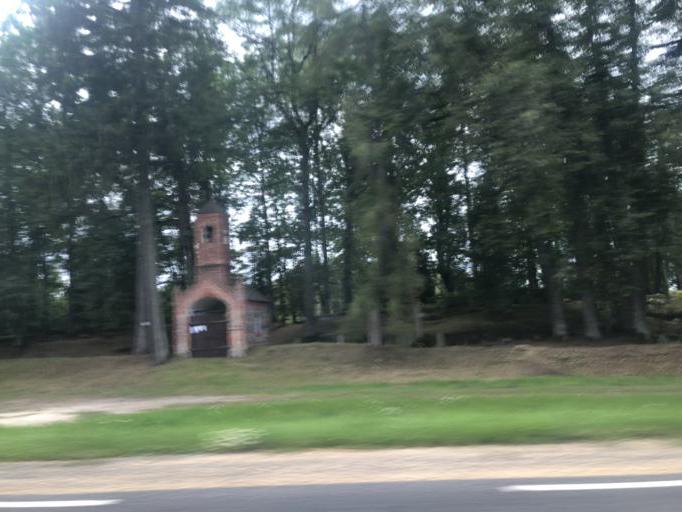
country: LV
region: Baldone
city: Baldone
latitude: 56.6901
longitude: 24.3909
